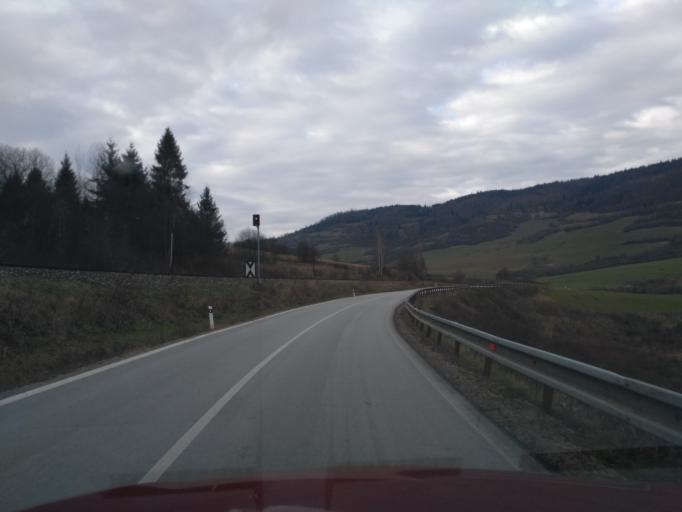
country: SK
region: Kosicky
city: Spisska Nova Ves
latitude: 48.8325
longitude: 20.6471
